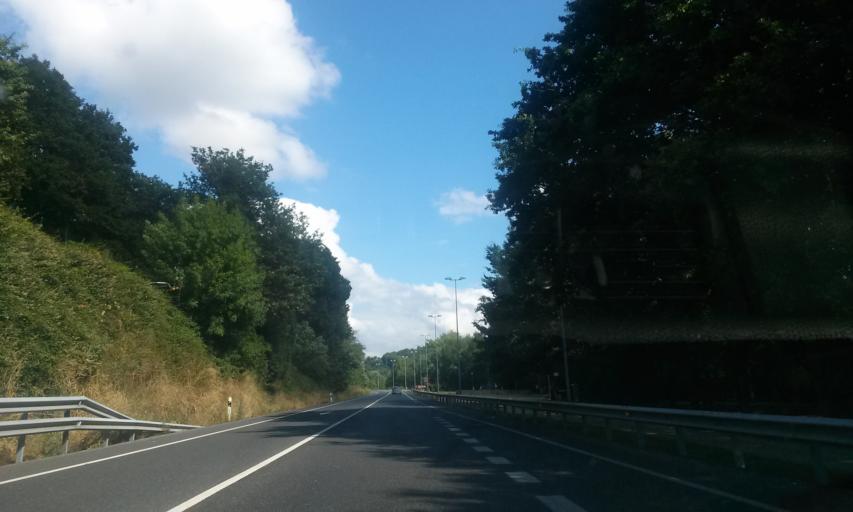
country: ES
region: Galicia
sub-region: Provincia de Lugo
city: Lugo
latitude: 42.9929
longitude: -7.5583
